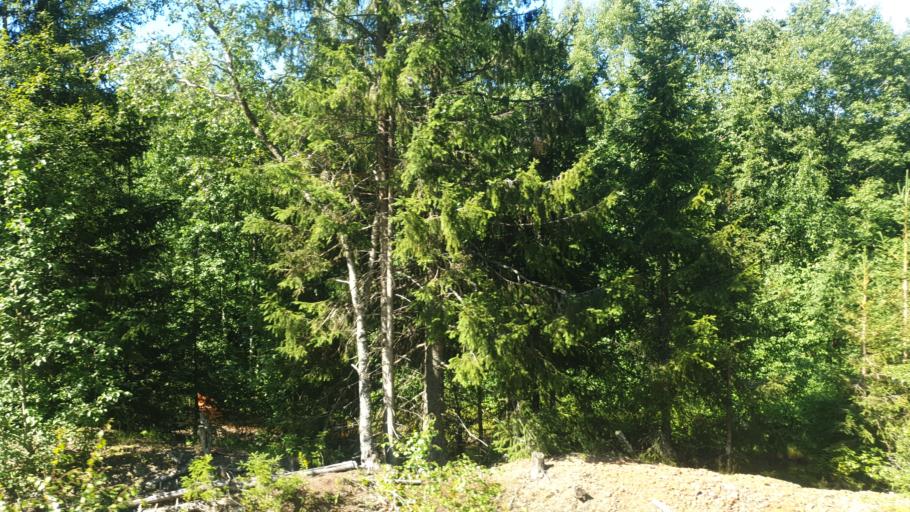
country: NO
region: Sor-Trondelag
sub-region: Meldal
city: Meldal
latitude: 63.1487
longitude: 9.7175
